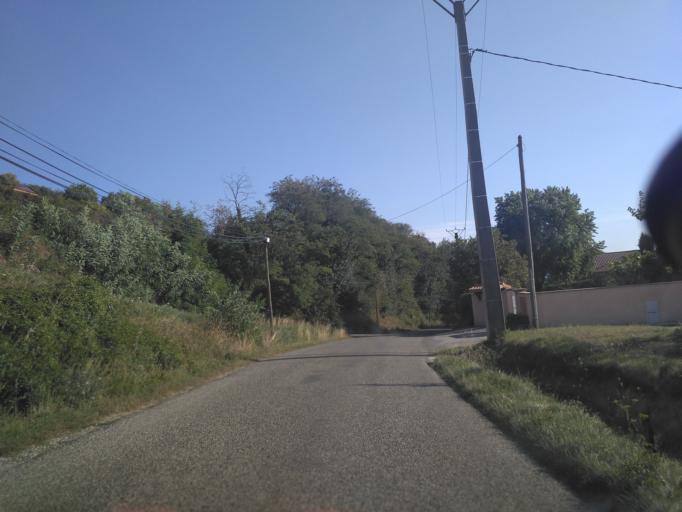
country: FR
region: Rhone-Alpes
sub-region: Departement de la Drome
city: Clerieux
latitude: 45.1283
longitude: 4.9881
